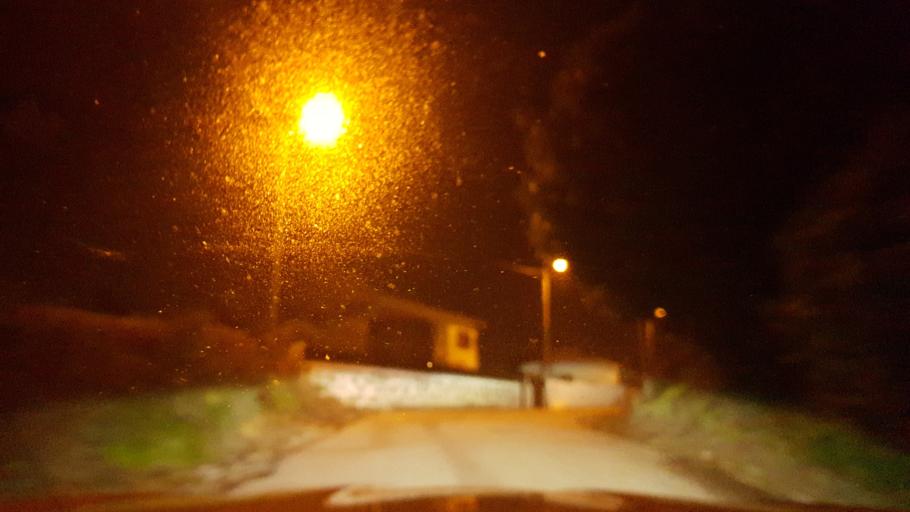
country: PT
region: Porto
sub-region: Matosinhos
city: Senhora da Hora
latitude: 41.2116
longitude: -8.6426
